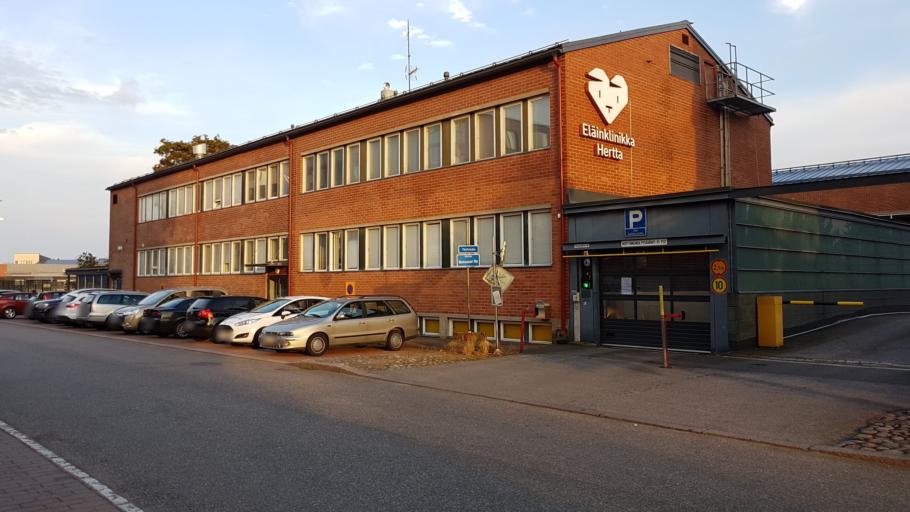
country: FI
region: Uusimaa
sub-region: Helsinki
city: Helsinki
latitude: 60.1903
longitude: 25.0264
